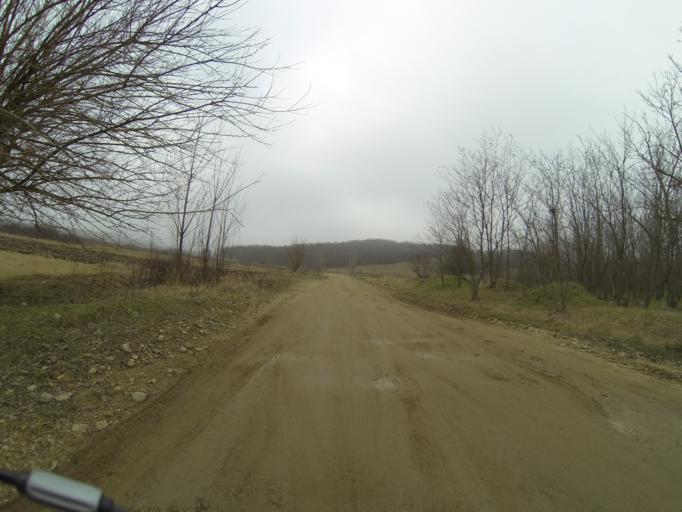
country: RO
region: Mehedinti
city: Padina Mica
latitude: 44.4857
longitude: 23.0290
